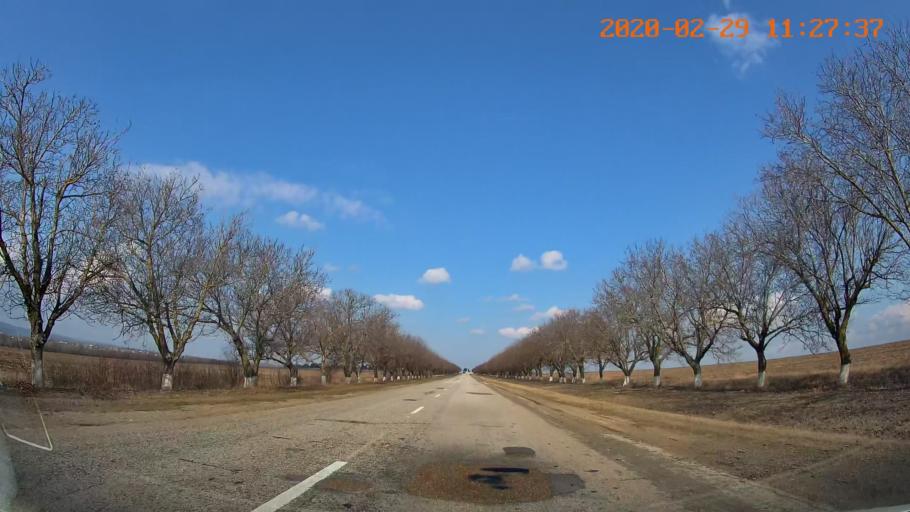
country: MD
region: Telenesti
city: Cocieri
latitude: 47.4711
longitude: 29.1417
